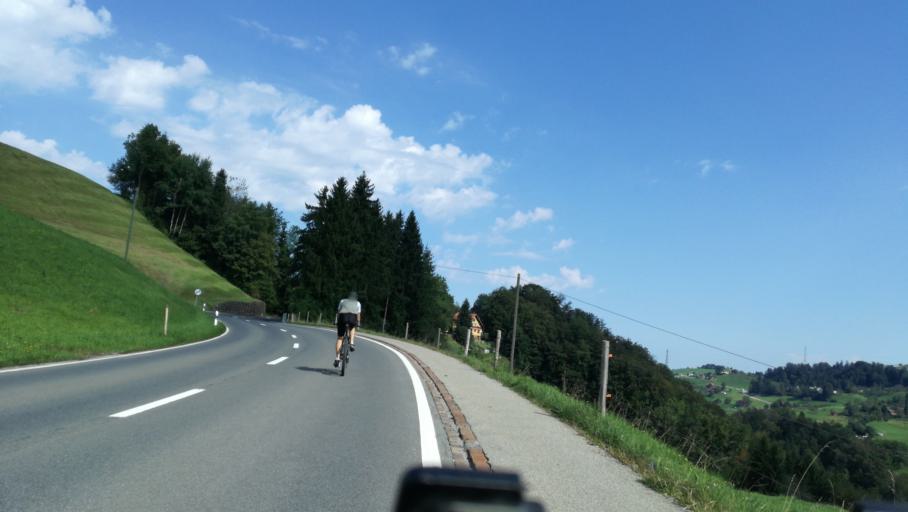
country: CH
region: Zug
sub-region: Zug
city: Unterageri
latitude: 47.1611
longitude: 8.5577
